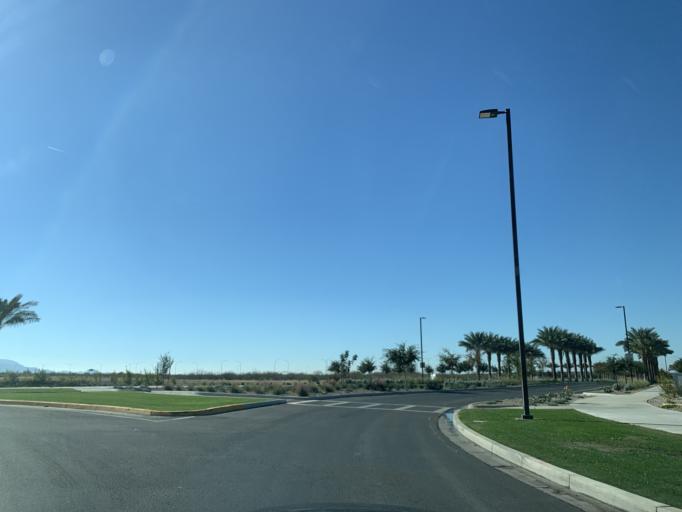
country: US
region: Arizona
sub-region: Maricopa County
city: Queen Creek
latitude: 33.3200
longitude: -111.6318
